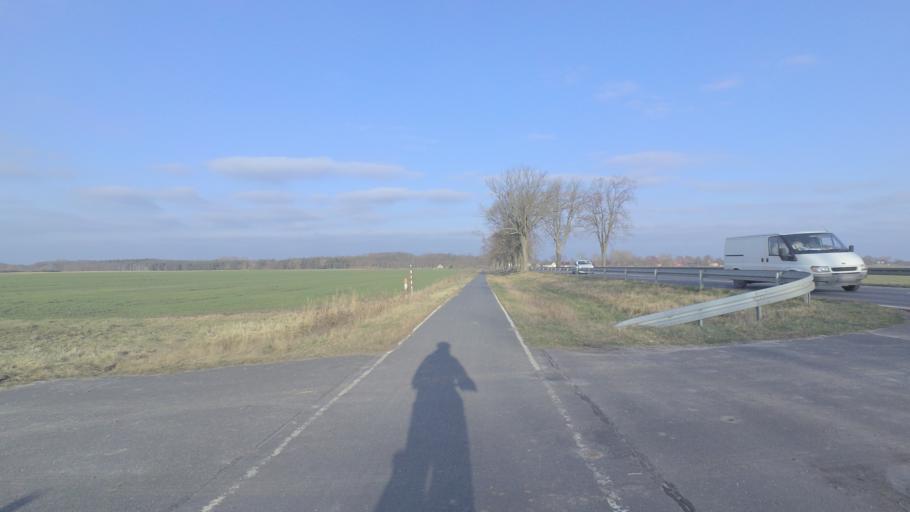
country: DE
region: Brandenburg
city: Rangsdorf
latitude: 52.2631
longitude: 13.4562
